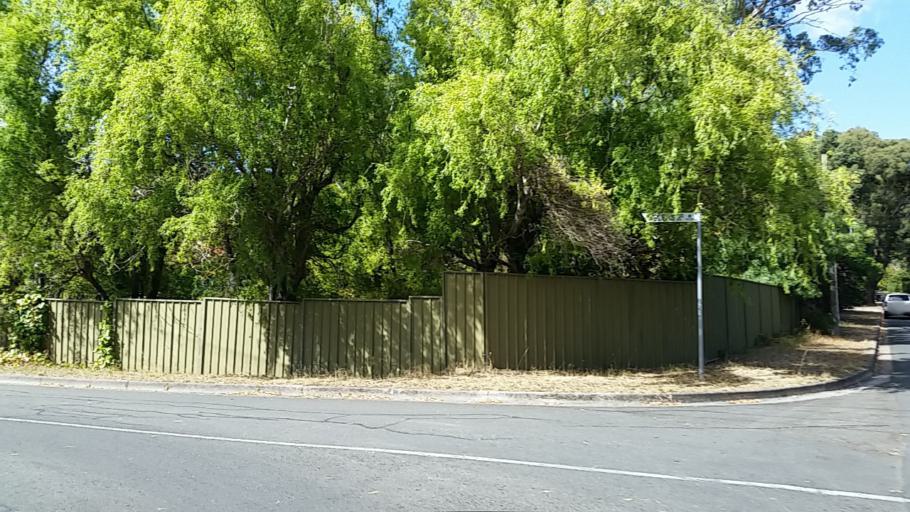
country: AU
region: South Australia
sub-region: Mount Barker
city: Hahndorf
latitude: -35.0304
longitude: 138.8174
